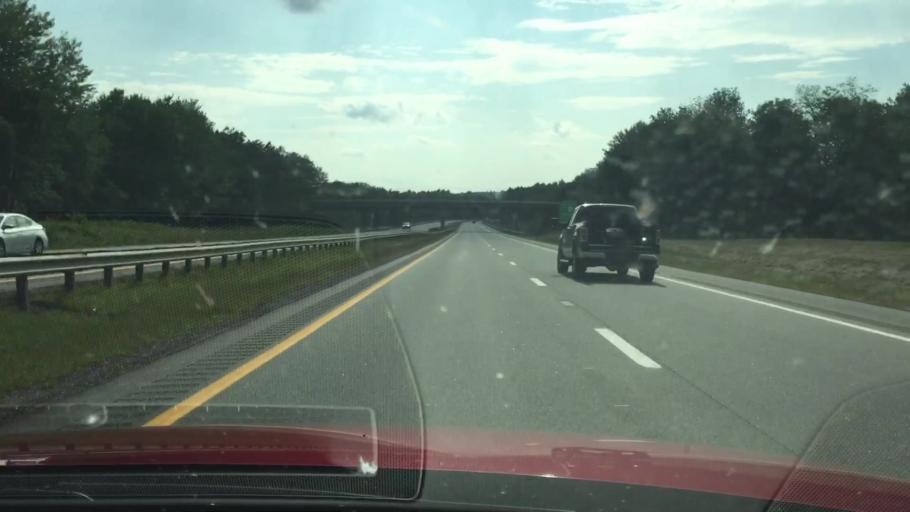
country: US
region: Maine
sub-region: Androscoggin County
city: Lisbon
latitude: 44.0718
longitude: -70.1368
